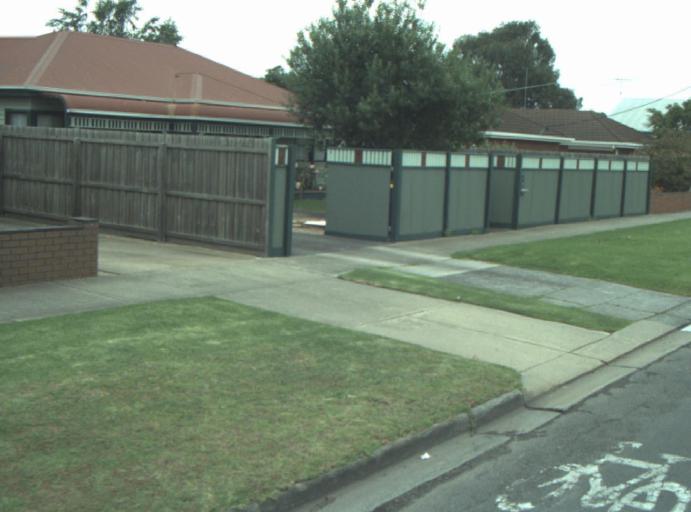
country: AU
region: Victoria
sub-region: Greater Geelong
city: East Geelong
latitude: -38.1593
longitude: 144.3863
